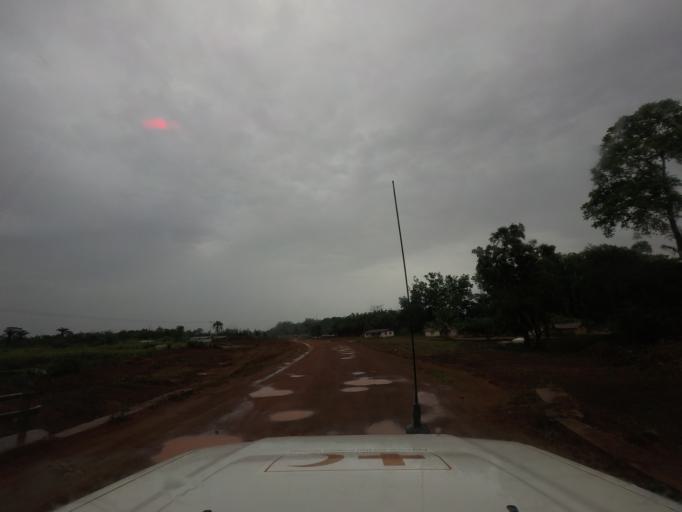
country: LR
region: Nimba
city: Sanniquellie
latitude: 7.2309
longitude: -8.9001
